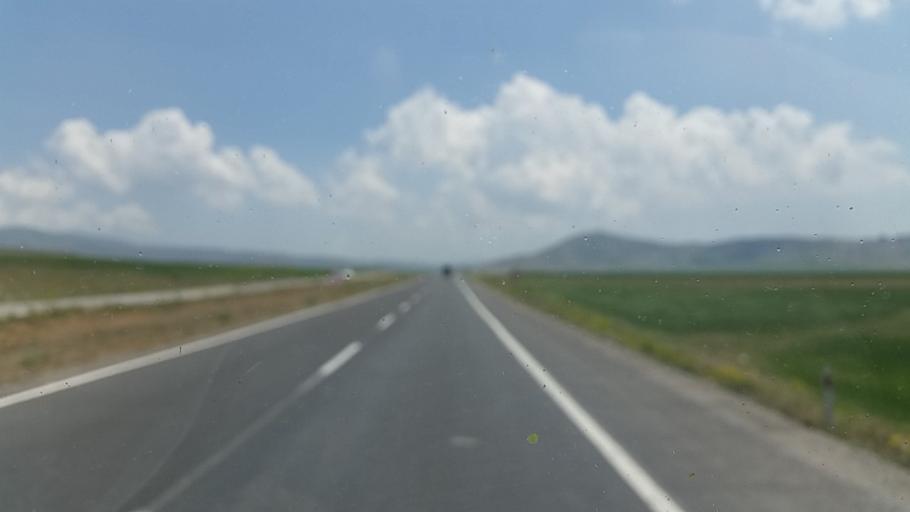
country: TR
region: Agri
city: Taslicay
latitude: 39.6295
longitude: 43.4363
